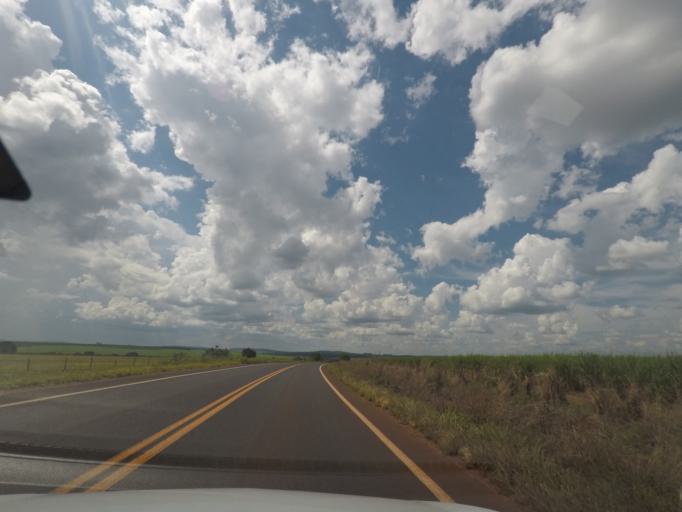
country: BR
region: Minas Gerais
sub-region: Conceicao Das Alagoas
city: Conceicao das Alagoas
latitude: -19.8282
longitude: -48.5917
